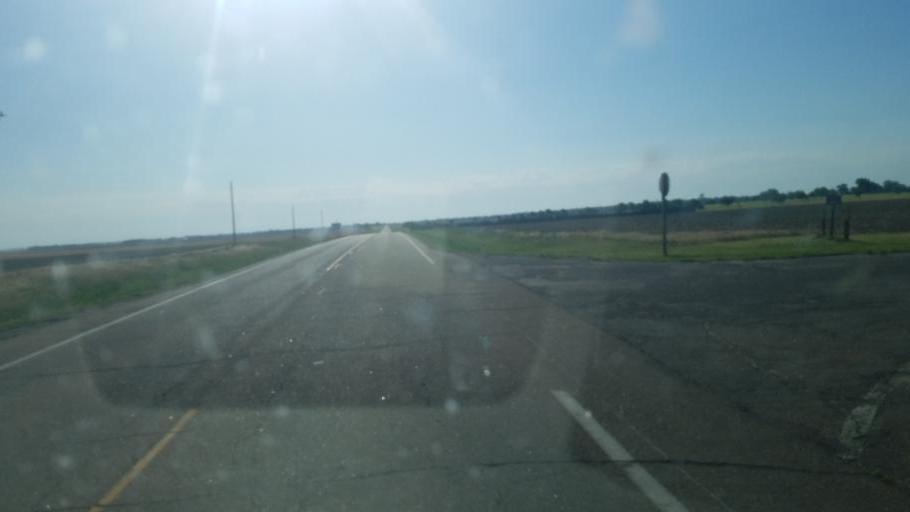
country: US
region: Kansas
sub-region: Pawnee County
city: Larned
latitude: 38.1888
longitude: -99.1413
